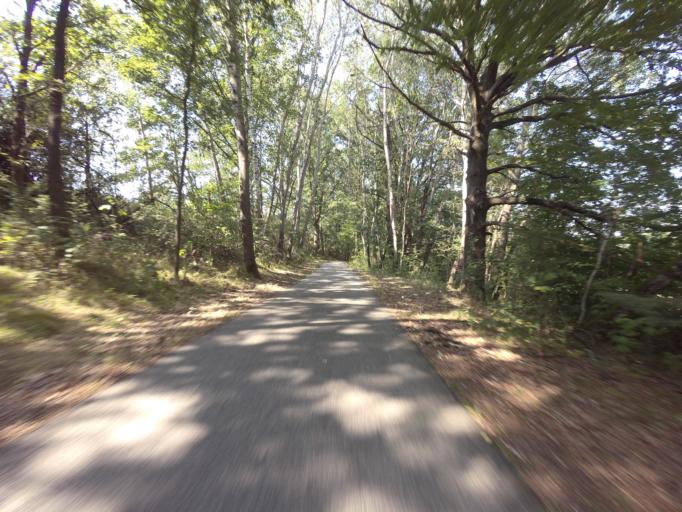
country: CZ
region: Jihocesky
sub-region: Okres Ceske Budejovice
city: Hluboka nad Vltavou
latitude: 49.1170
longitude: 14.4584
